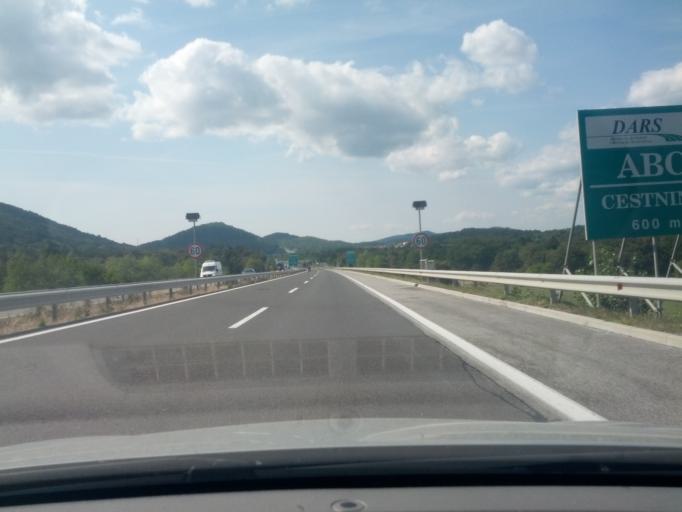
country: SI
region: Sezana
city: Sezana
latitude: 45.7132
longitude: 13.9034
